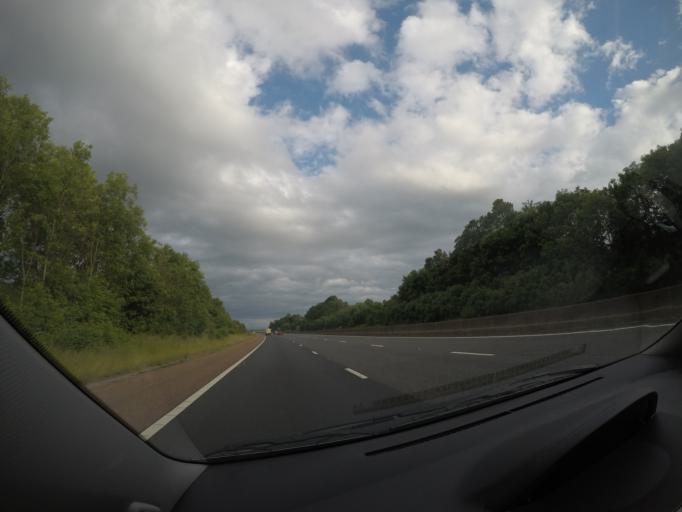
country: GB
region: England
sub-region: Cumbria
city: Penrith
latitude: 54.6824
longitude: -2.7873
